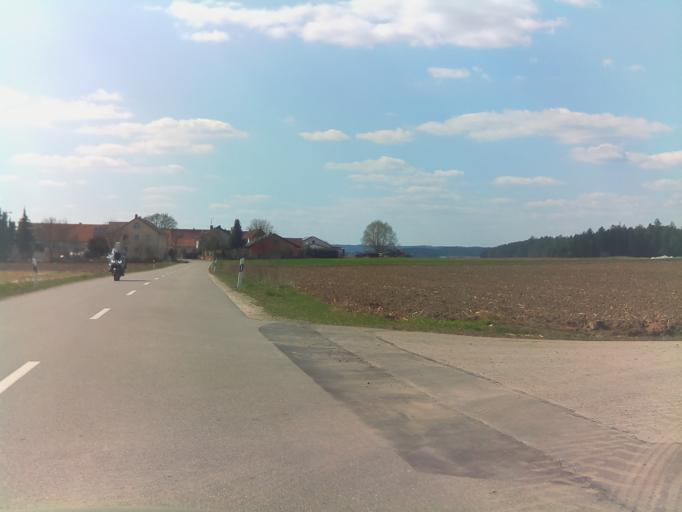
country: DE
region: Bavaria
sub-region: Swabia
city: Inchenhofen
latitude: 48.5376
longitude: 11.1580
